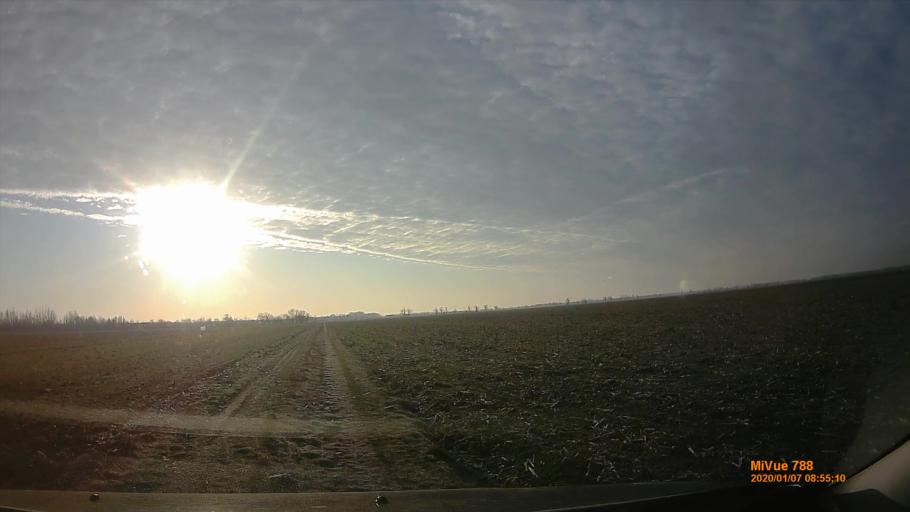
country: HU
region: Gyor-Moson-Sopron
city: Rajka
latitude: 47.9924
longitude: 17.1756
